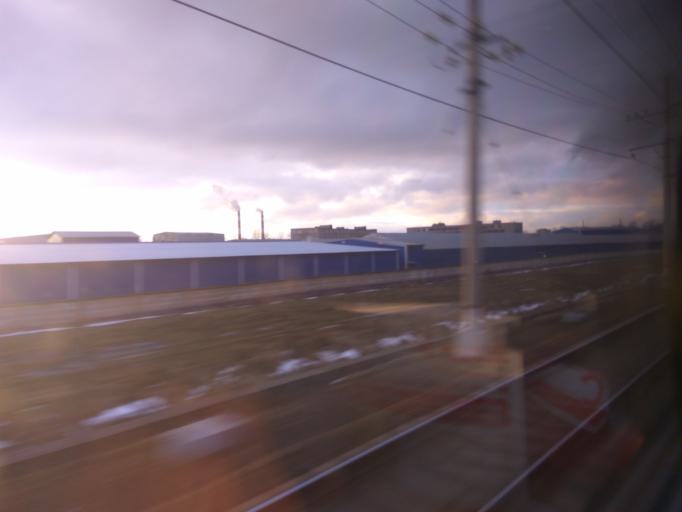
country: RU
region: St.-Petersburg
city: Kupchino
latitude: 59.8884
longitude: 30.3960
